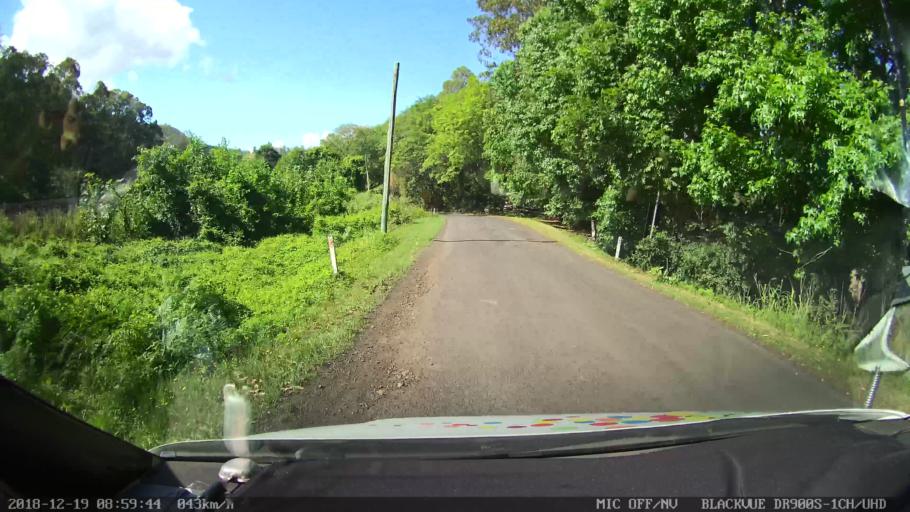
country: AU
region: New South Wales
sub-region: Kyogle
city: Kyogle
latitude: -28.4281
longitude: 152.9579
